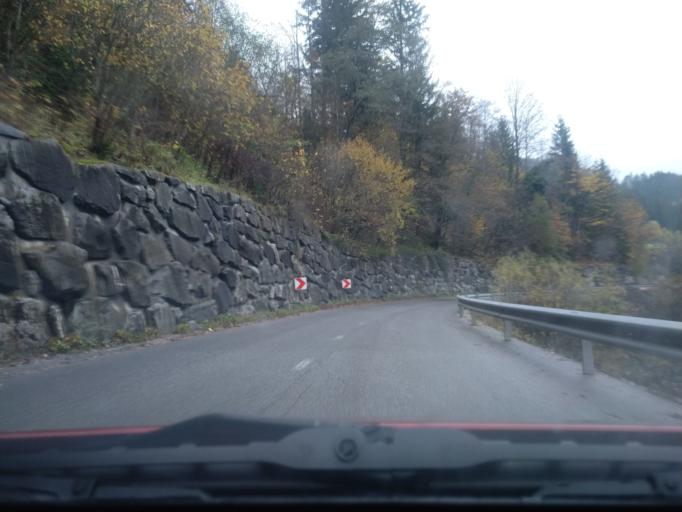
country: SI
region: Luce
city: Luce
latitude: 46.3606
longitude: 14.7600
